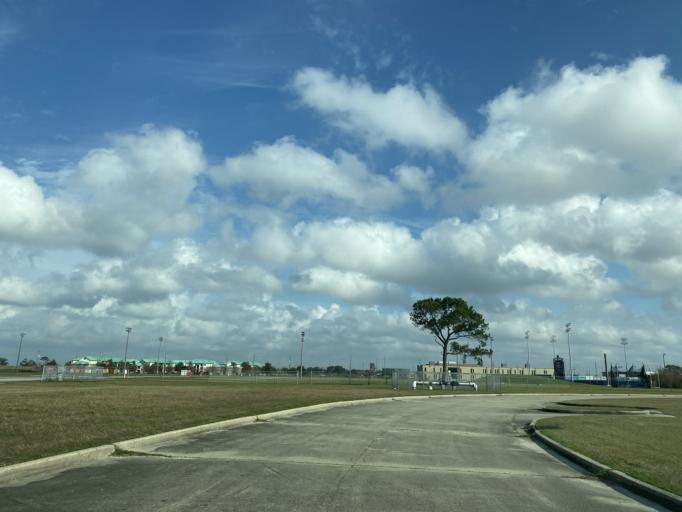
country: US
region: Louisiana
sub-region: Orleans Parish
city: New Orleans
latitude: 30.0321
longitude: -90.0502
